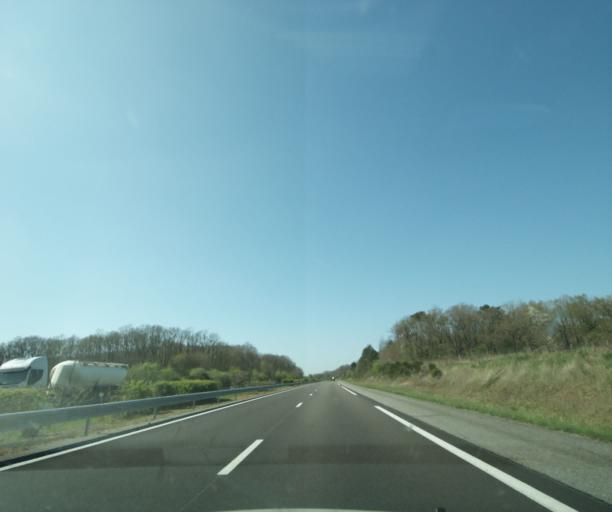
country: FR
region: Centre
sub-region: Departement du Loiret
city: Bonny-sur-Loire
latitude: 47.6134
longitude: 2.8180
